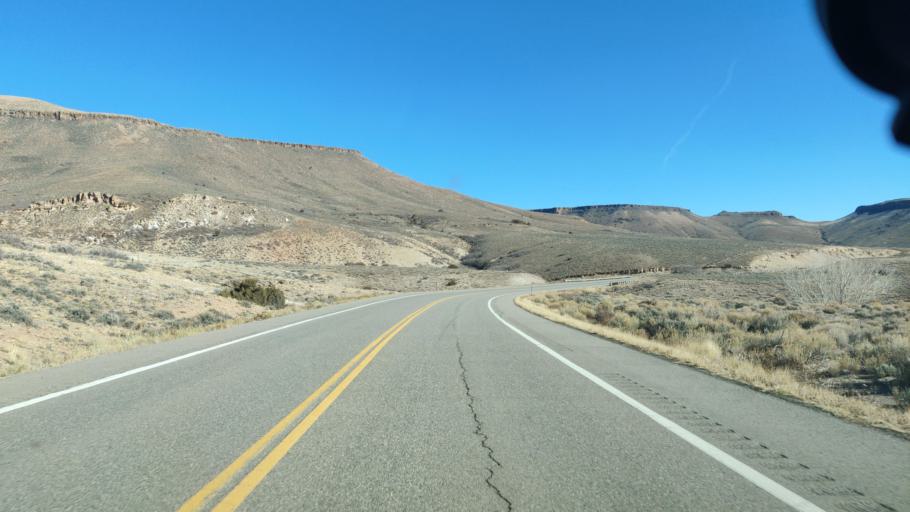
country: US
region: Colorado
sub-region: Gunnison County
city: Gunnison
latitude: 38.4812
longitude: -107.1917
